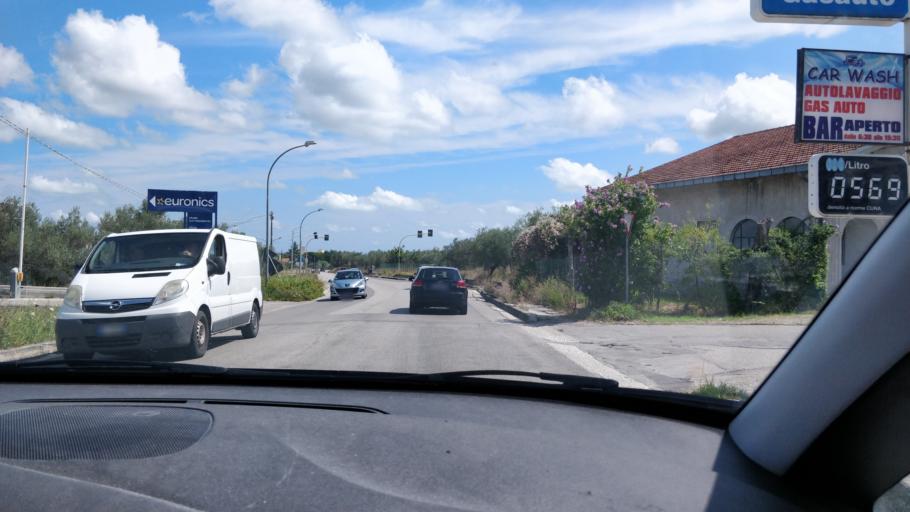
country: IT
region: Abruzzo
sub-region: Provincia di Chieti
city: Treglio
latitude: 42.2467
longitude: 14.4183
